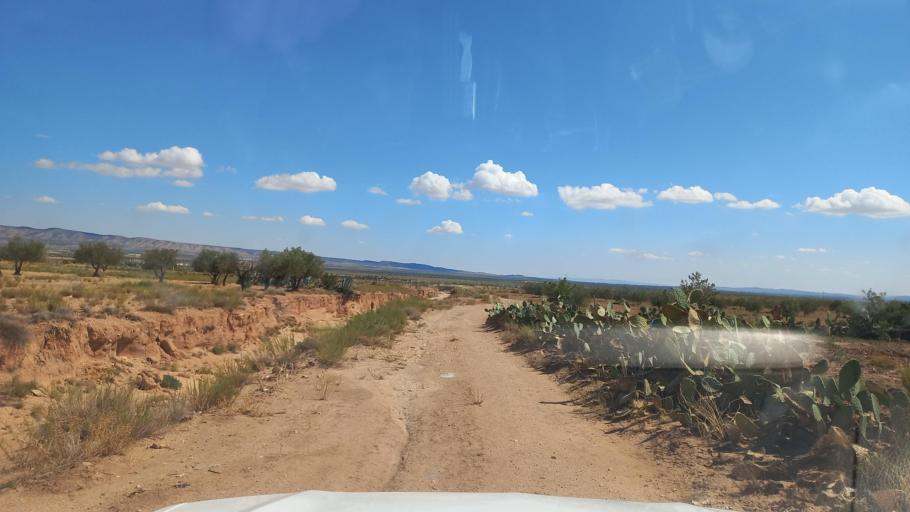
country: TN
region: Al Qasrayn
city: Sbiba
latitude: 35.3548
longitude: 9.0161
